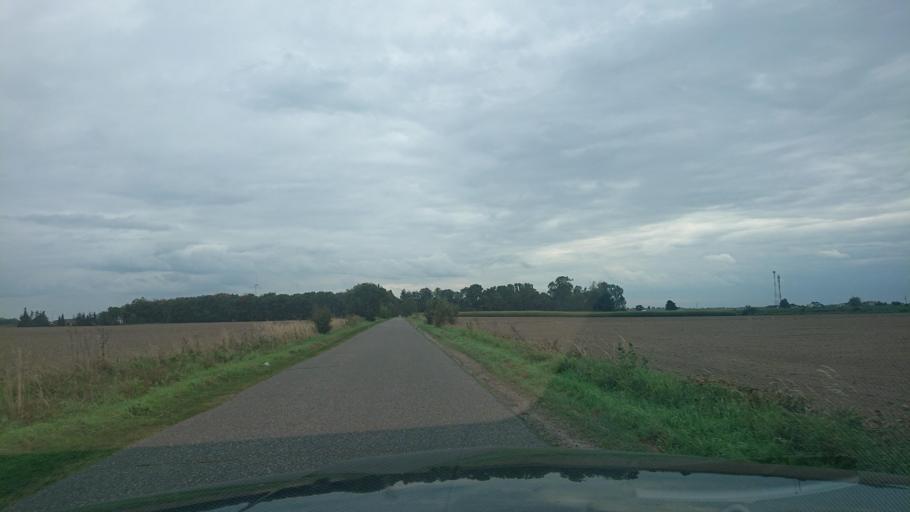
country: PL
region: Greater Poland Voivodeship
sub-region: Powiat gnieznienski
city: Niechanowo
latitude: 52.4612
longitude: 17.6203
